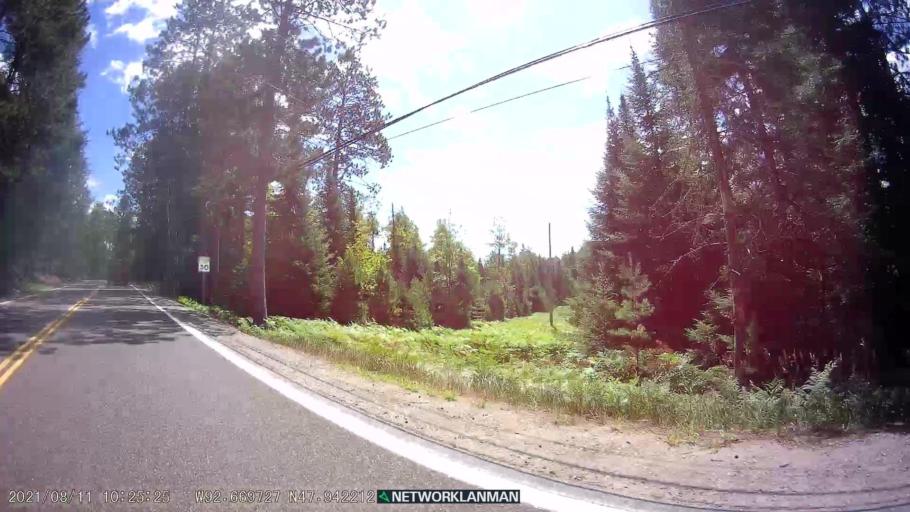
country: US
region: Minnesota
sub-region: Saint Louis County
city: Mountain Iron
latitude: 47.9422
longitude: -92.6698
